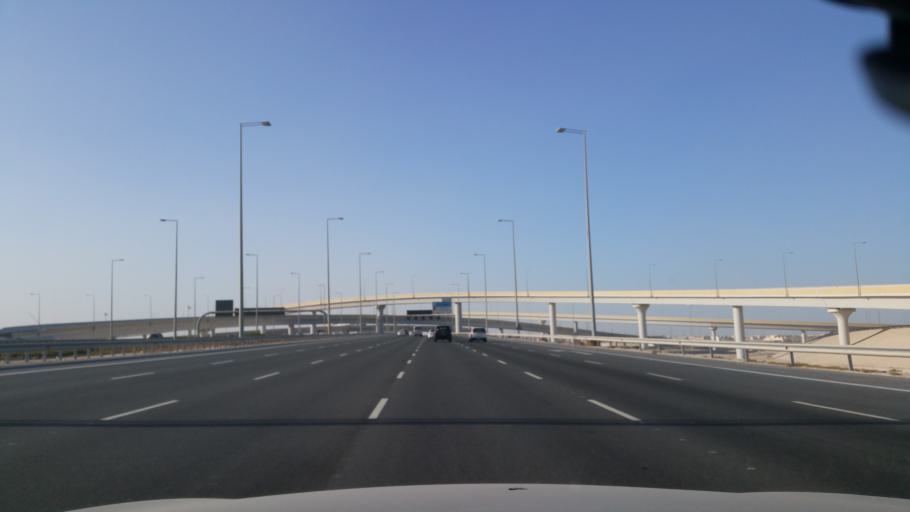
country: QA
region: Al Wakrah
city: Al Wukayr
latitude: 25.1991
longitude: 51.5432
